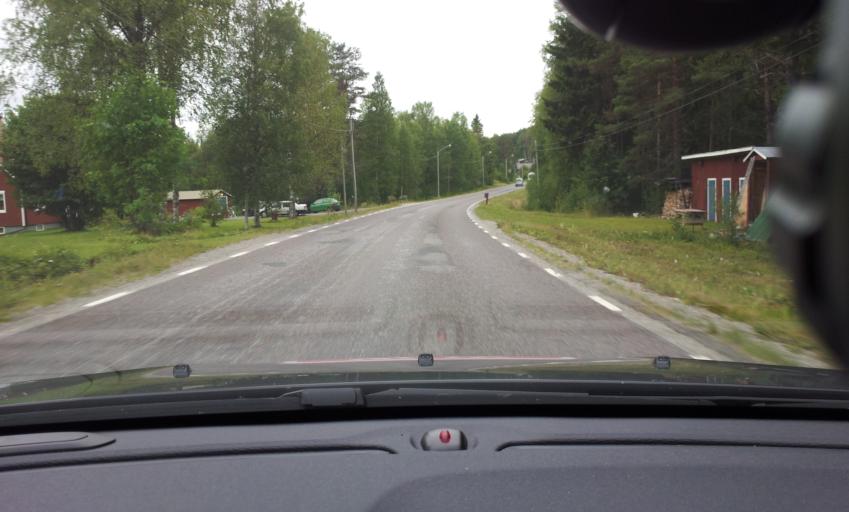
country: SE
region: Jaemtland
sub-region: Braecke Kommun
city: Braecke
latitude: 63.0402
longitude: 15.2803
